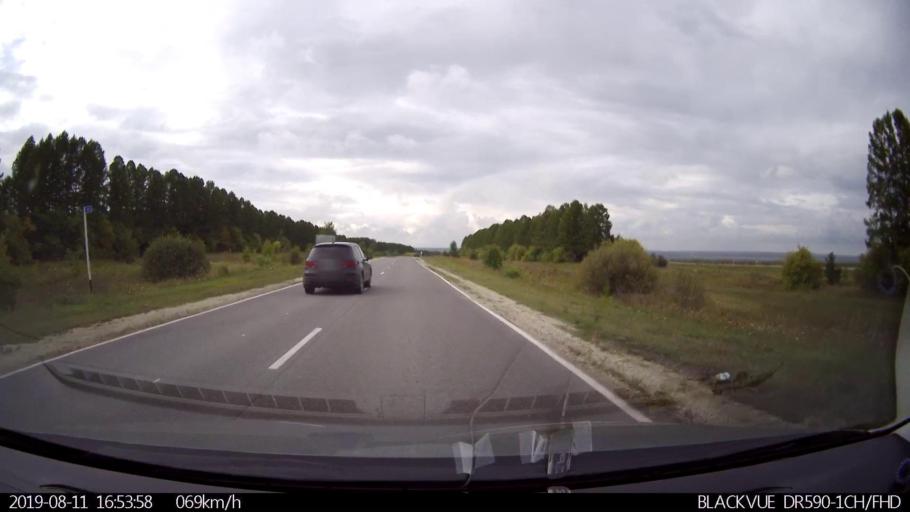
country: RU
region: Ulyanovsk
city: Mayna
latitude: 54.2680
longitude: 47.6680
